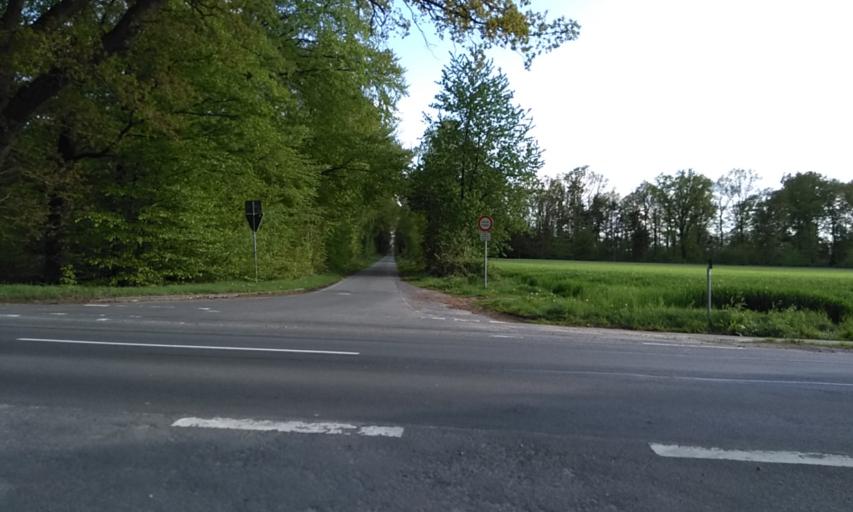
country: DE
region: Lower Saxony
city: Regesbostel
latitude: 53.4042
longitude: 9.6561
